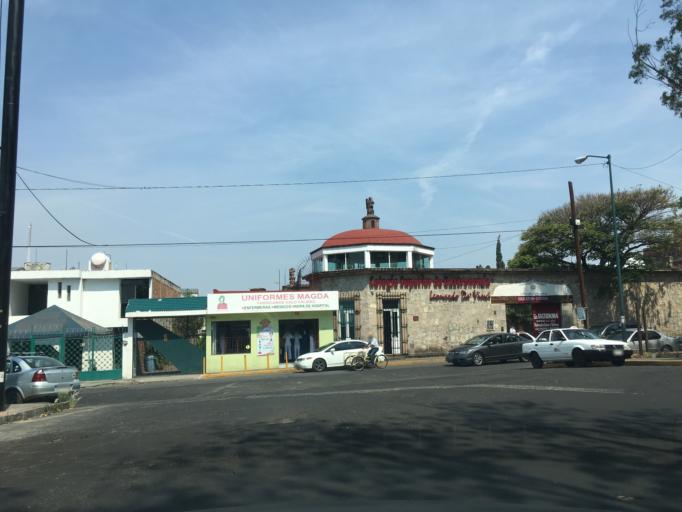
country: MX
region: Michoacan
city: Morelia
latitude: 19.6968
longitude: -101.1822
